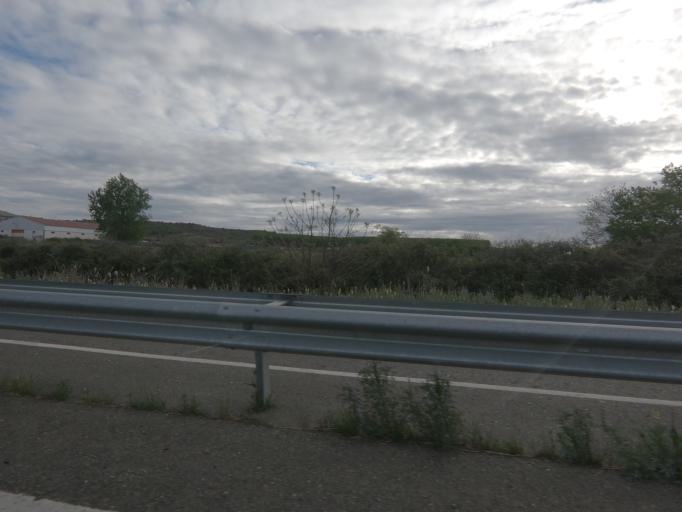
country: ES
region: Extremadura
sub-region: Provincia de Caceres
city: Coria
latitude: 39.9651
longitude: -6.5180
